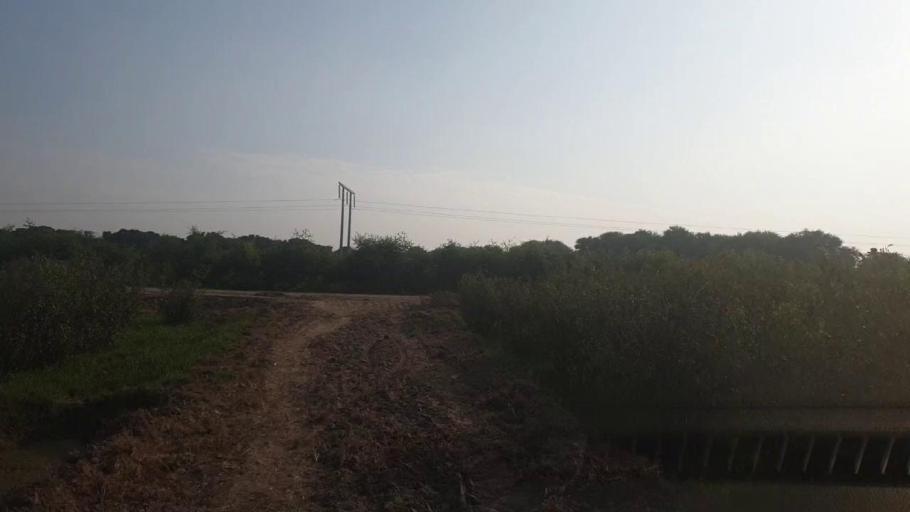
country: PK
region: Sindh
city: Tando Jam
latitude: 25.4255
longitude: 68.4621
